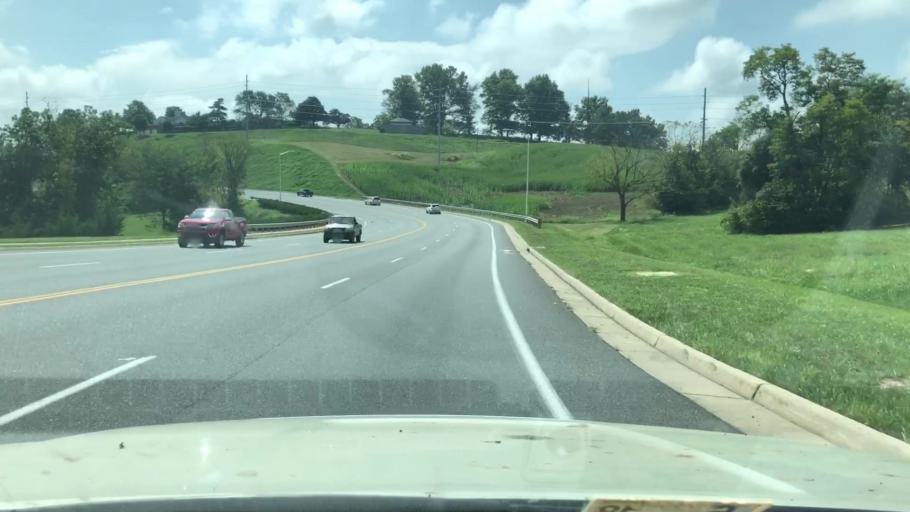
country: US
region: Virginia
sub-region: City of Harrisonburg
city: Harrisonburg
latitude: 38.4279
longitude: -78.9003
